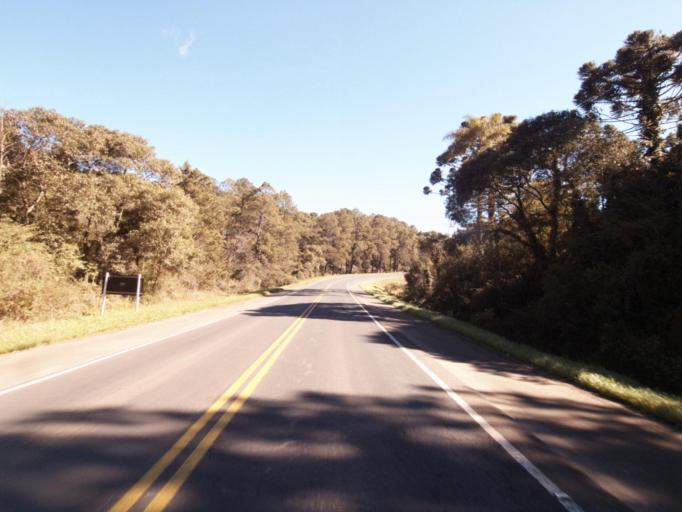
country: BR
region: Santa Catarina
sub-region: Joacaba
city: Joacaba
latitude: -27.1614
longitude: -51.5719
